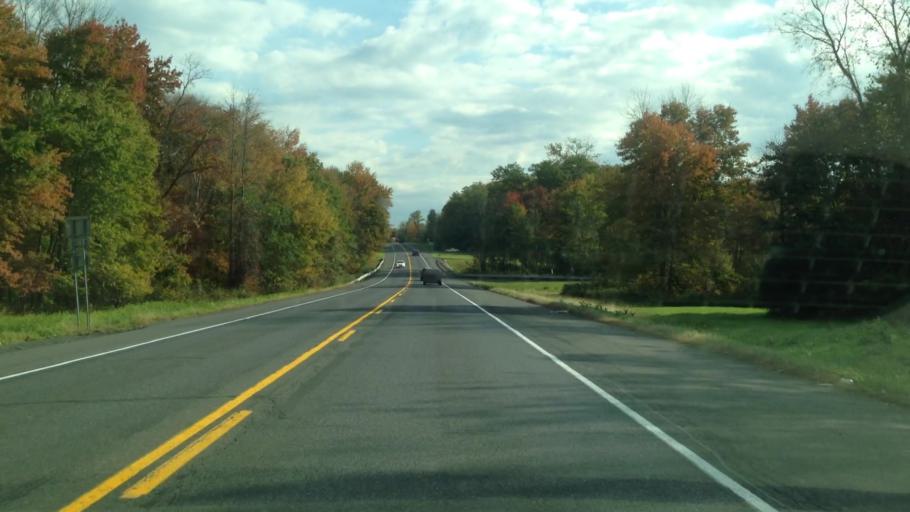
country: US
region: New York
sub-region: Ulster County
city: Highland
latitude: 41.7384
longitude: -74.0143
